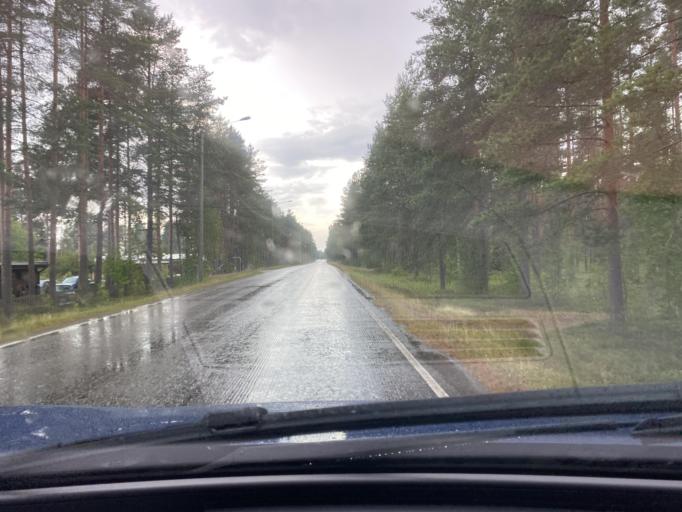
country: FI
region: Central Ostrobothnia
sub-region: Kaustinen
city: Veteli
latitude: 63.4696
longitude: 23.8195
